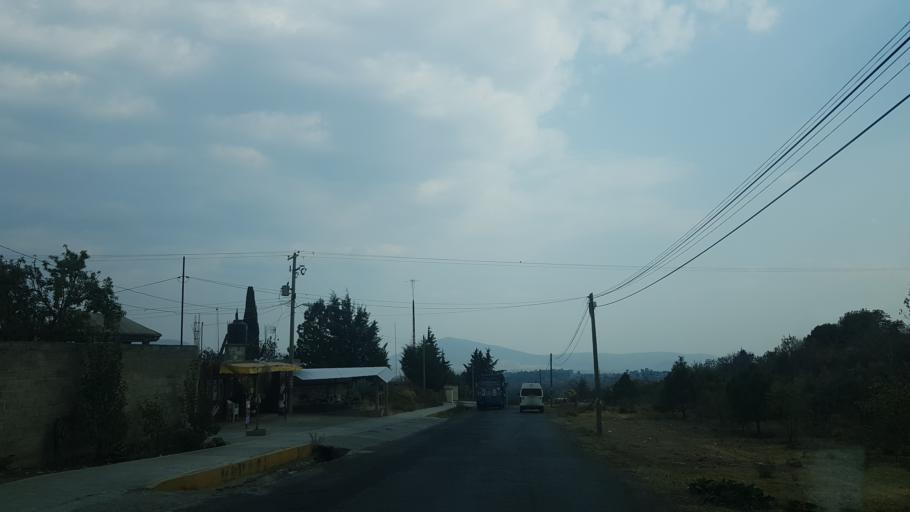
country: MX
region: Puebla
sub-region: Santa Isabel Cholula
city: San Martin Tlamapa
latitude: 18.9739
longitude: -98.3946
